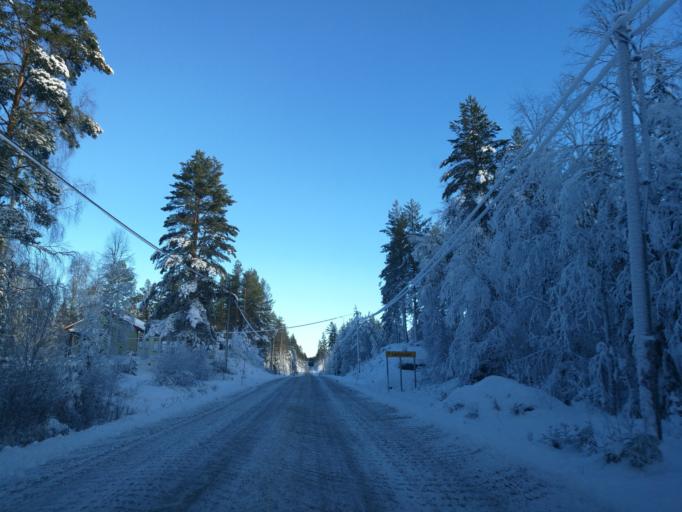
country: NO
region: Hedmark
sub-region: Grue
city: Kirkenaer
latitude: 60.4576
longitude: 12.5250
